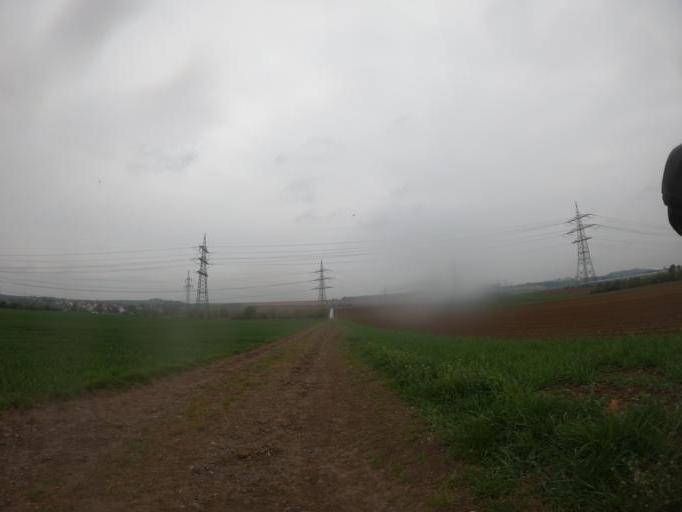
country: DE
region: Baden-Wuerttemberg
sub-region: Regierungsbezirk Stuttgart
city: Oberriexingen
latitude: 48.8964
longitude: 9.0236
